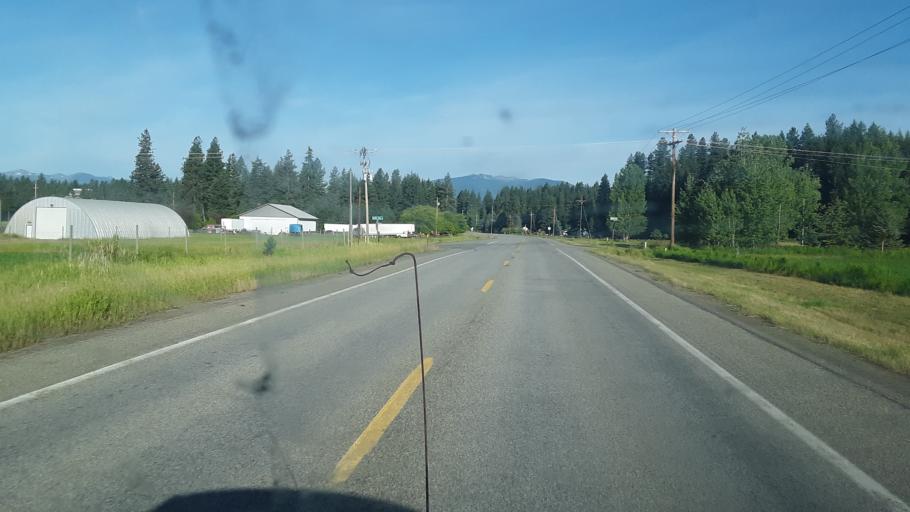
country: US
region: Idaho
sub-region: Boundary County
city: Bonners Ferry
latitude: 48.7311
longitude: -116.2423
